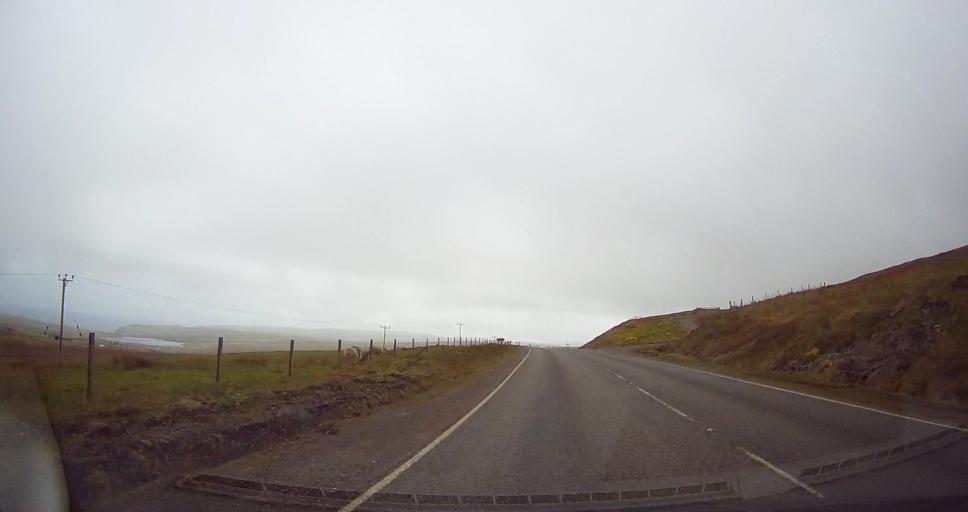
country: GB
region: Scotland
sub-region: Shetland Islands
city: Sandwick
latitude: 59.9580
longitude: -1.2860
